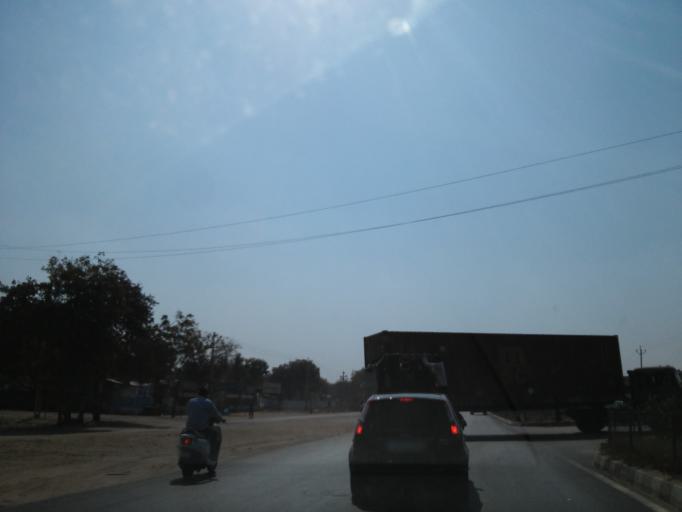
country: IN
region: Gujarat
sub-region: Gandhinagar
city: Adalaj
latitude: 23.1571
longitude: 72.5544
